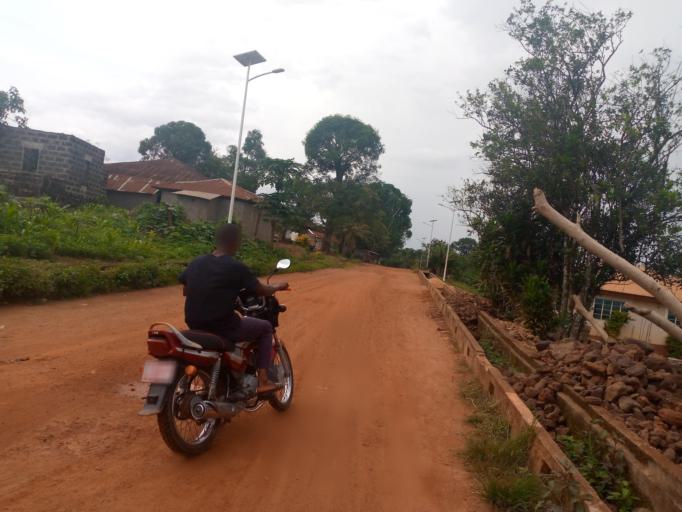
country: SL
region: Southern Province
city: Mogbwemo
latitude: 7.6075
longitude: -12.1759
